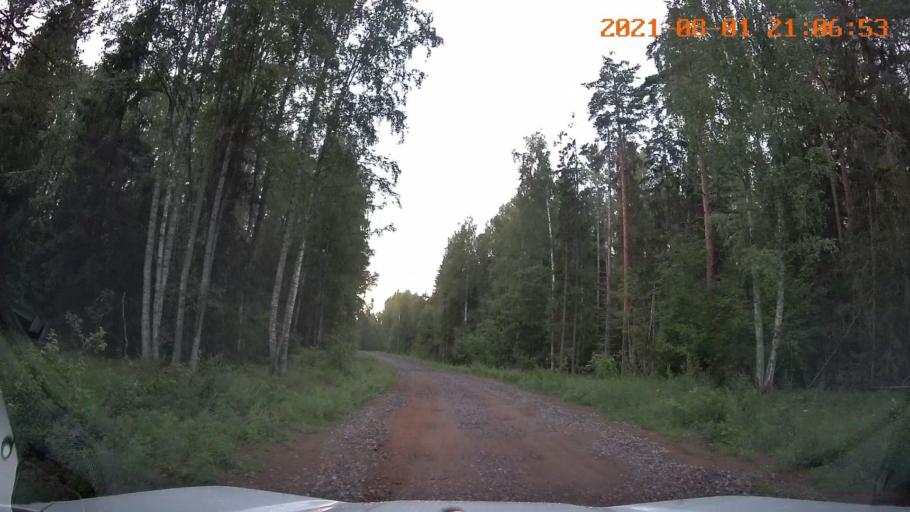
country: RU
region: Leningrad
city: Syas'stroy
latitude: 60.5029
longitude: 32.6495
